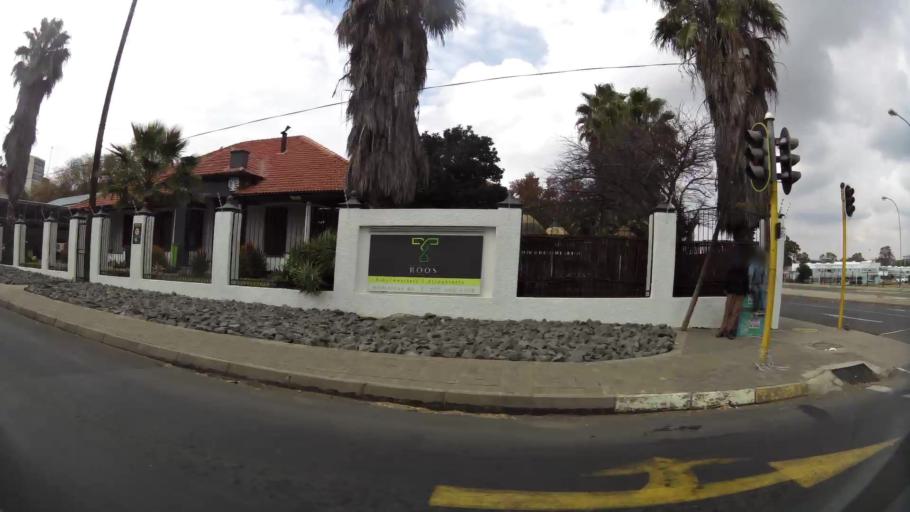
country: ZA
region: Orange Free State
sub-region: Mangaung Metropolitan Municipality
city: Bloemfontein
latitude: -29.1099
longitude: 26.2201
